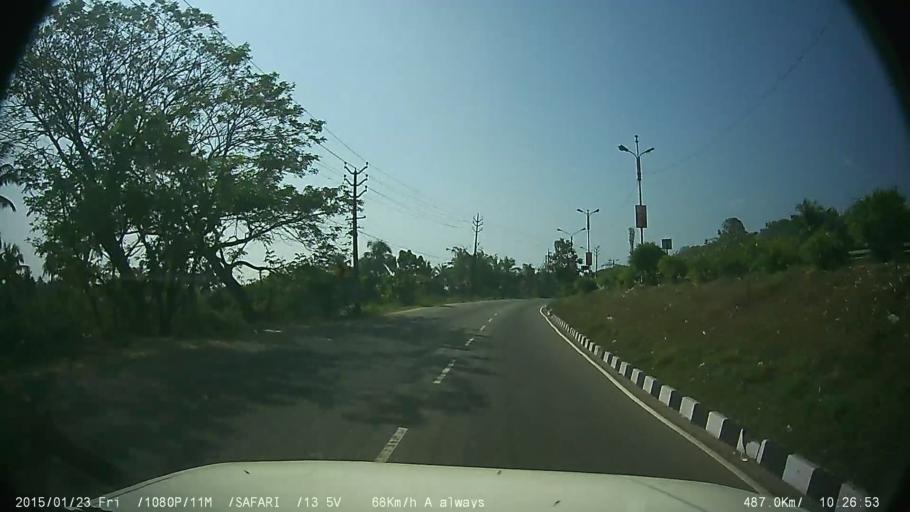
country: IN
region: Kerala
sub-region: Ernakulam
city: Angamali
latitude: 10.1809
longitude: 76.3798
